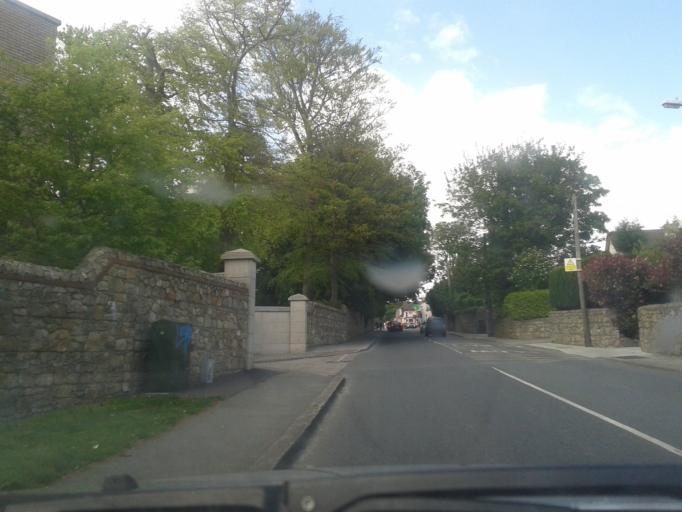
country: IE
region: Leinster
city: Loughlinstown
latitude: 53.2513
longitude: -6.1231
